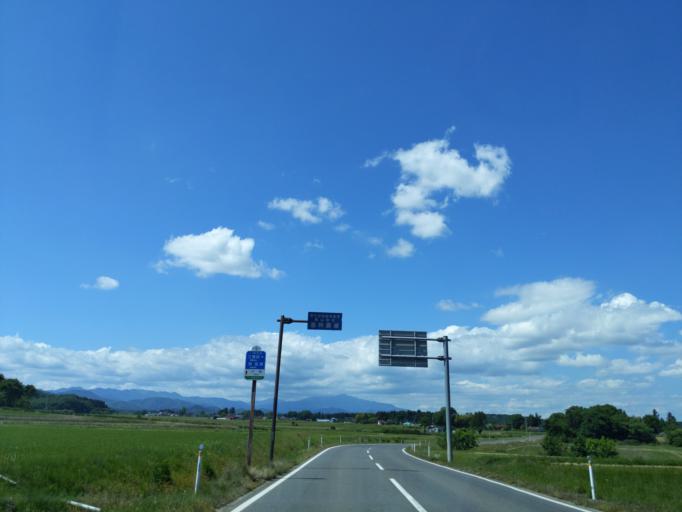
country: JP
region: Fukushima
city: Koriyama
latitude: 37.3755
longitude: 140.2940
